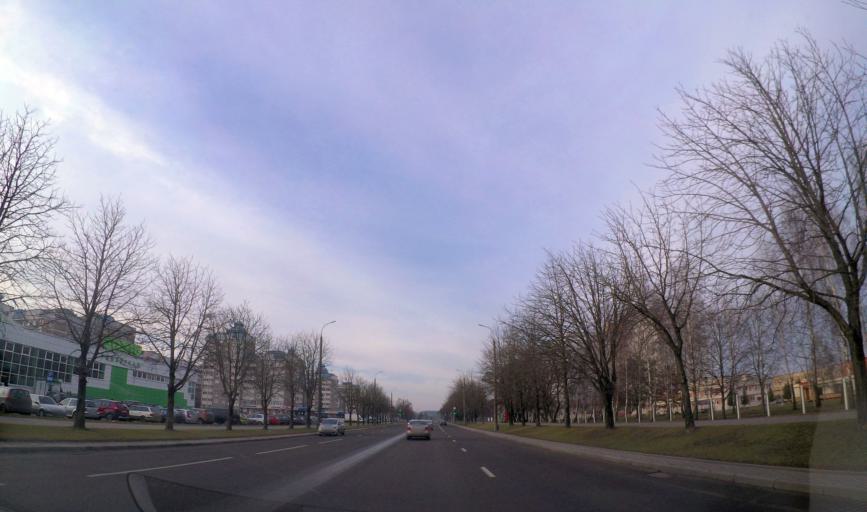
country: BY
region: Grodnenskaya
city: Hrodna
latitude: 53.6724
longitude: 23.7996
